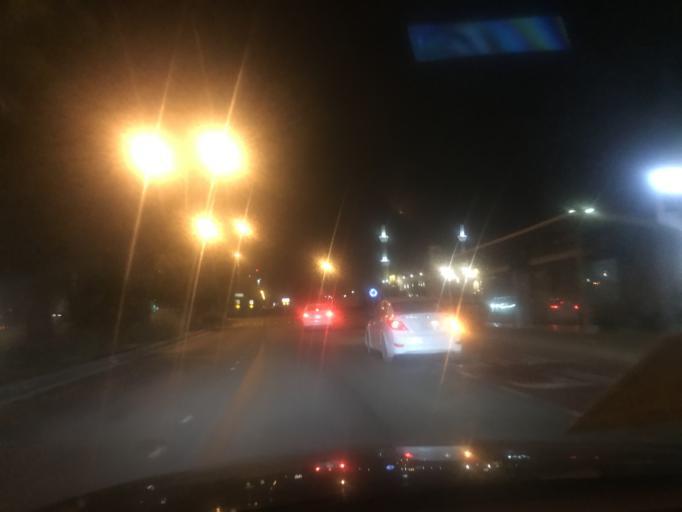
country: SA
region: Ar Riyad
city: Riyadh
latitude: 24.6929
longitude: 46.6055
